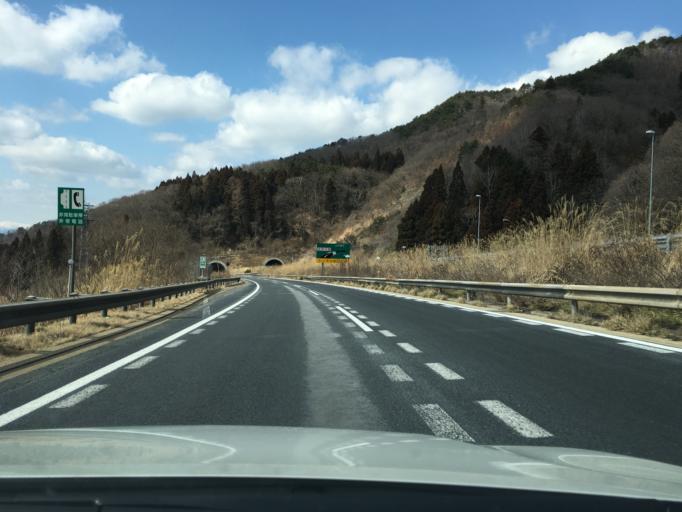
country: JP
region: Yamagata
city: Yamagata-shi
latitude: 38.2430
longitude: 140.4037
